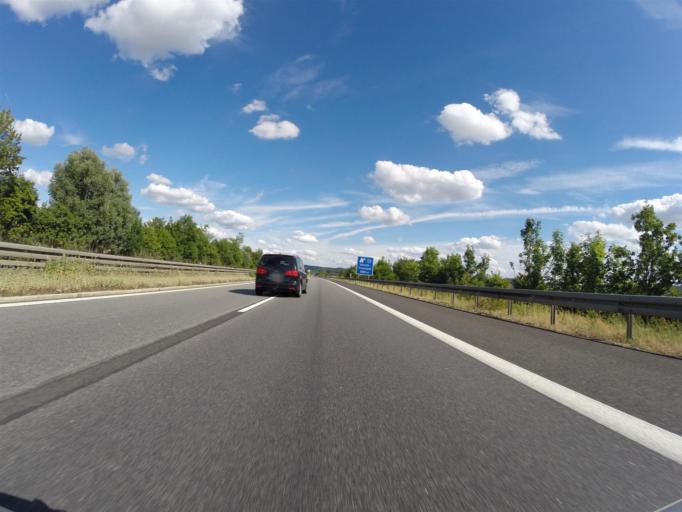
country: DE
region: Bavaria
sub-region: Upper Franconia
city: Viereth-Trunstadt
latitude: 49.9420
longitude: 10.7644
